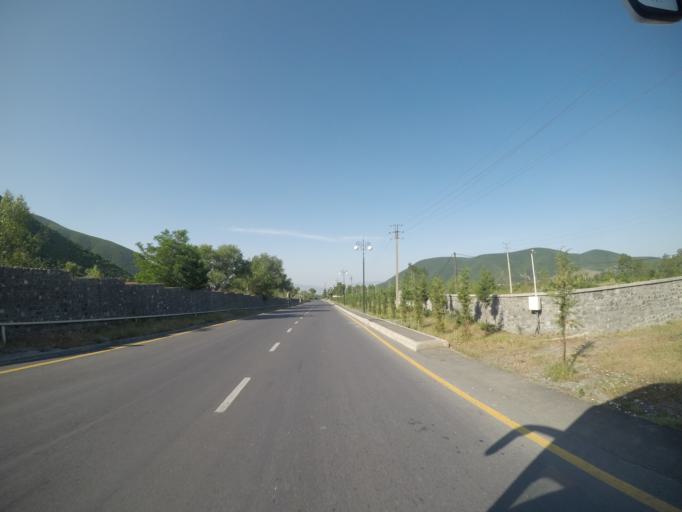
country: AZ
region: Shaki City
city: Sheki
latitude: 41.2362
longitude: 47.1813
